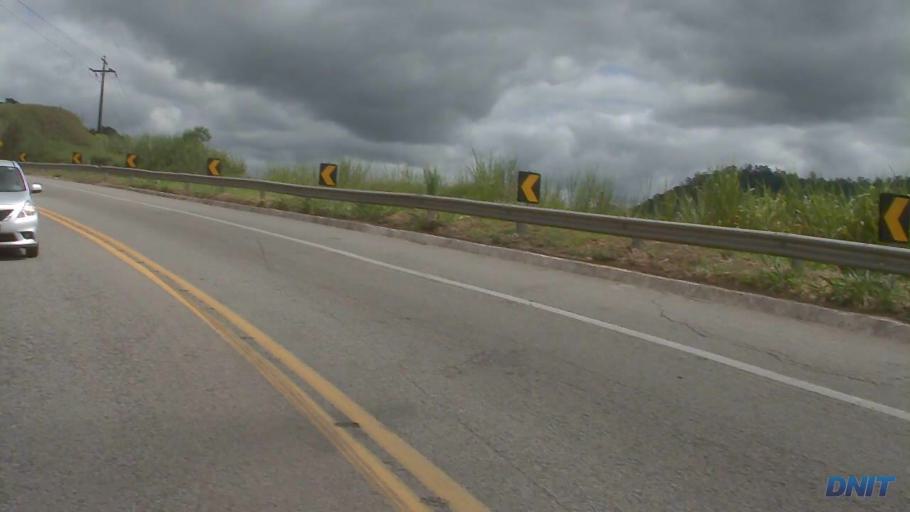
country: BR
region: Minas Gerais
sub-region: Joao Monlevade
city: Joao Monlevade
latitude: -19.8504
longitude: -43.1527
